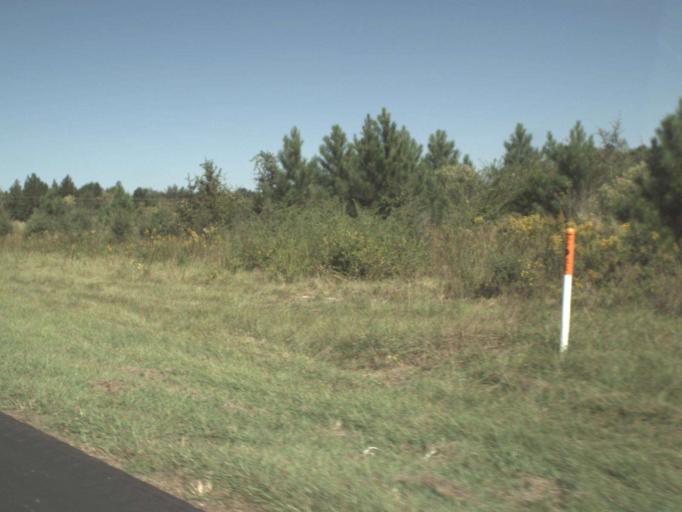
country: US
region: Alabama
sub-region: Covington County
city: Florala
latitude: 30.9420
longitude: -86.2830
